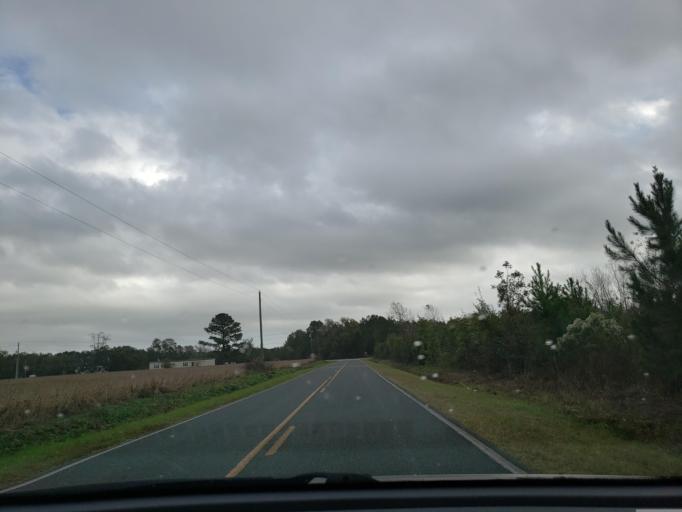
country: US
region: North Carolina
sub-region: Onslow County
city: Richlands
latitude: 34.7364
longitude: -77.6235
